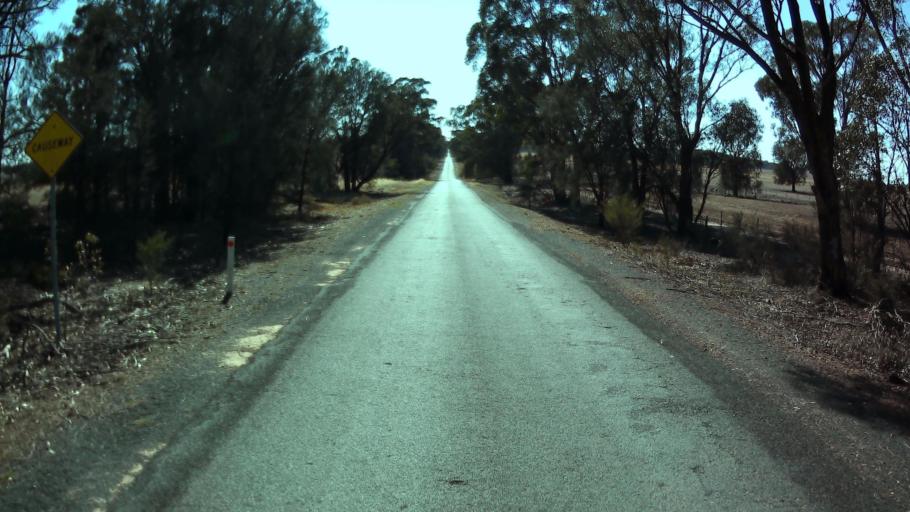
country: AU
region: New South Wales
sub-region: Weddin
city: Grenfell
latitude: -33.7825
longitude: 147.9669
